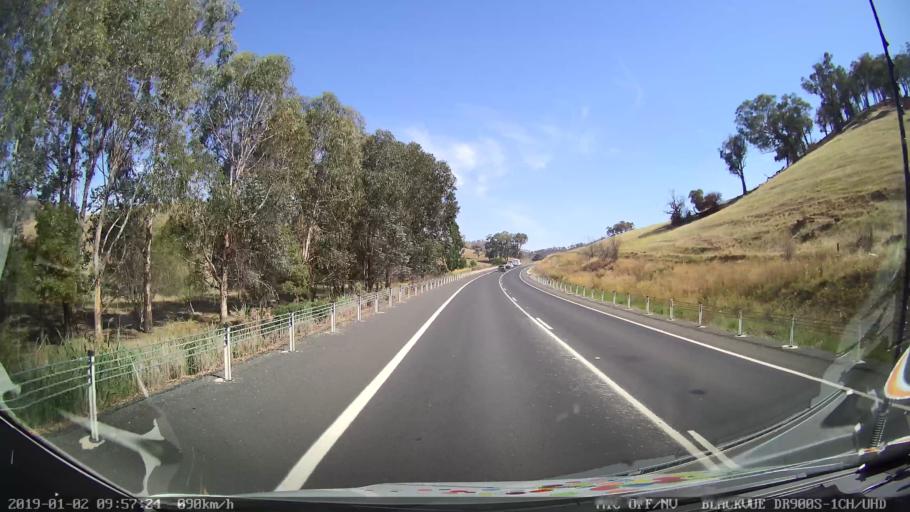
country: AU
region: New South Wales
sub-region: Tumut Shire
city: Tumut
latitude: -35.2059
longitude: 148.1662
